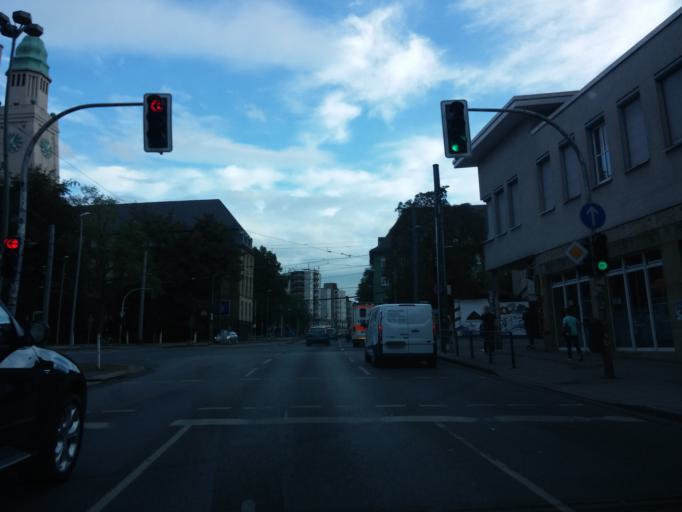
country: DE
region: North Rhine-Westphalia
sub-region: Regierungsbezirk Munster
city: Gladbeck
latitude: 51.5781
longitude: 7.0560
